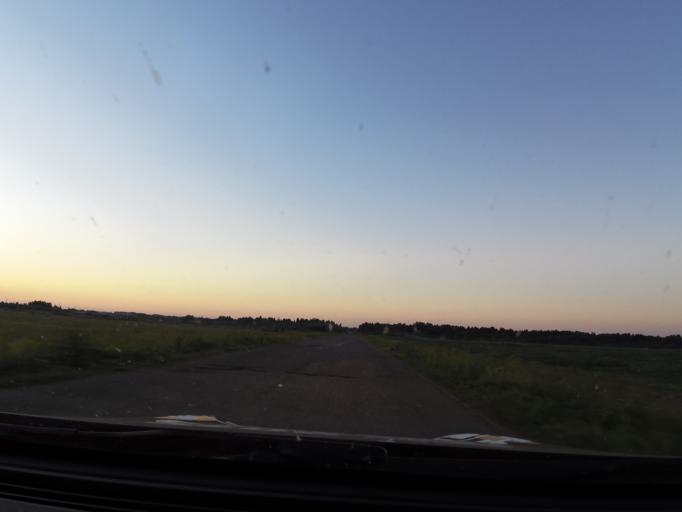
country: RU
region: Kostroma
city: Buy
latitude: 58.3792
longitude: 41.2142
